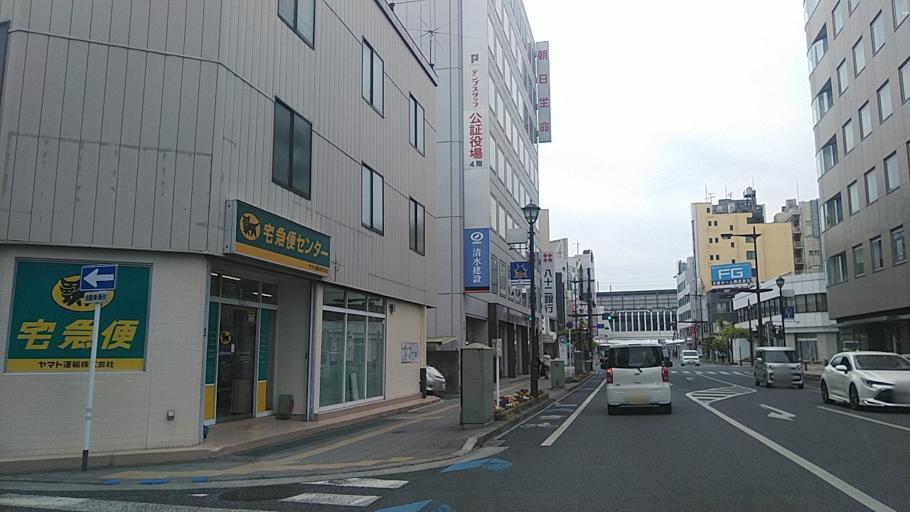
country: JP
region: Saitama
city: Kumagaya
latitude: 36.1422
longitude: 139.3905
